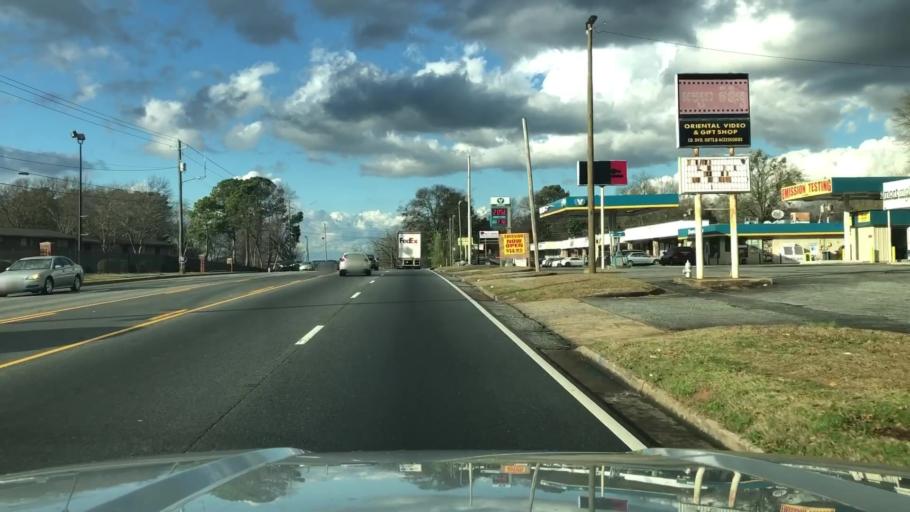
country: US
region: Georgia
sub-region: Clayton County
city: Riverdale
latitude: 33.6098
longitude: -84.4363
